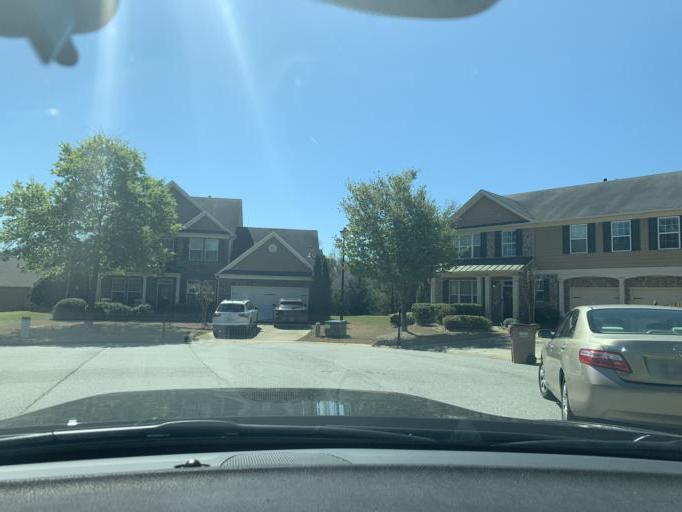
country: US
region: Georgia
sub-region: Forsyth County
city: Cumming
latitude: 34.1419
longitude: -84.2031
